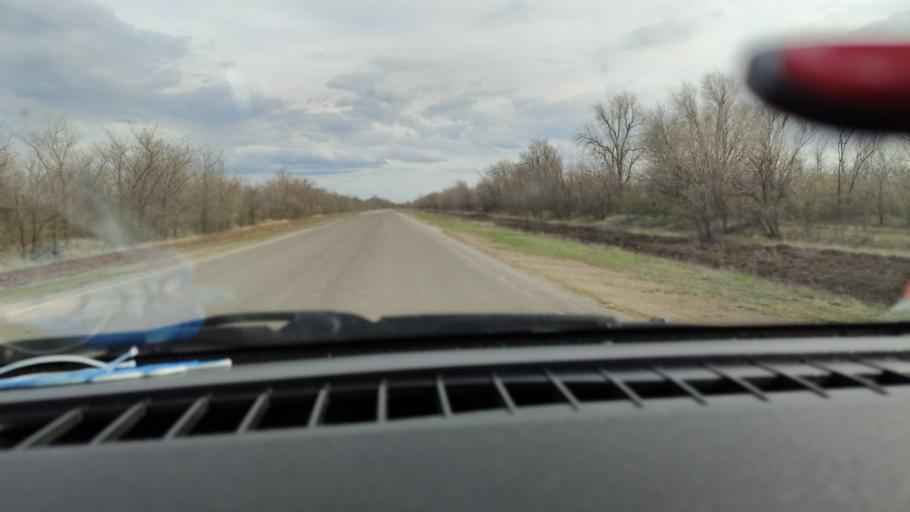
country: RU
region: Saratov
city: Rovnoye
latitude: 50.9803
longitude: 46.1159
